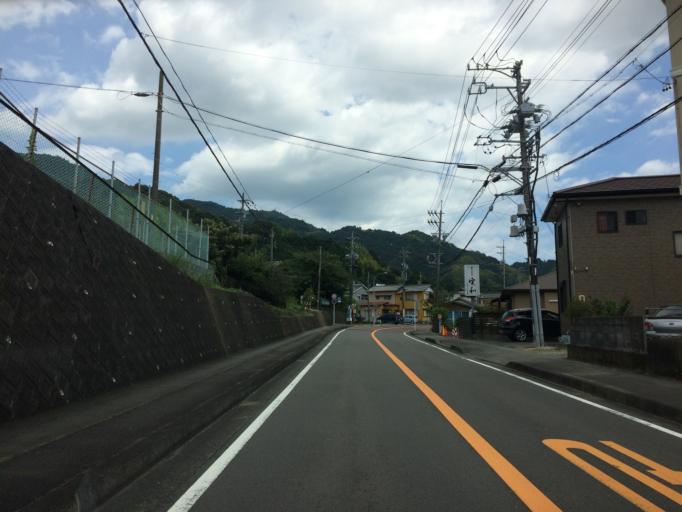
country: JP
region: Shizuoka
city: Fujieda
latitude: 34.9057
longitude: 138.2898
